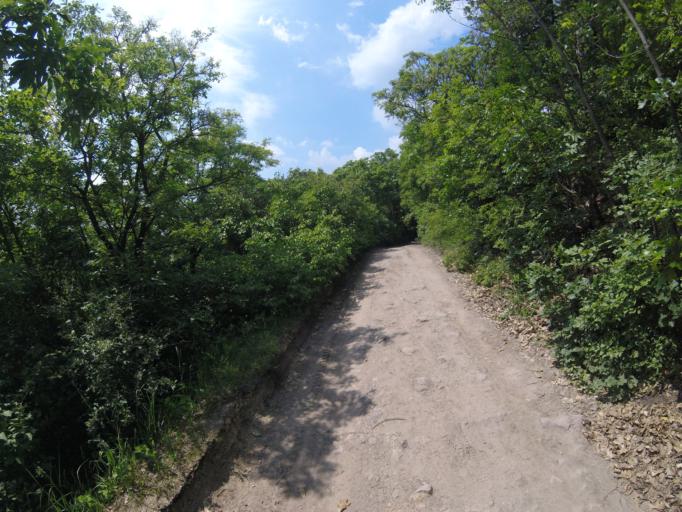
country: HU
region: Pest
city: Nagykovacsi
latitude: 47.6769
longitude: 19.0206
